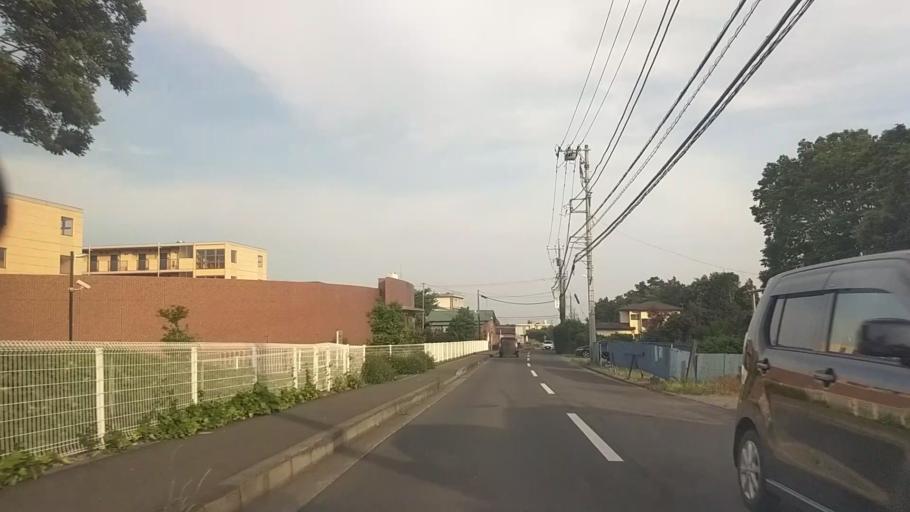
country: JP
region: Kanagawa
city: Odawara
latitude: 35.3224
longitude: 139.1102
